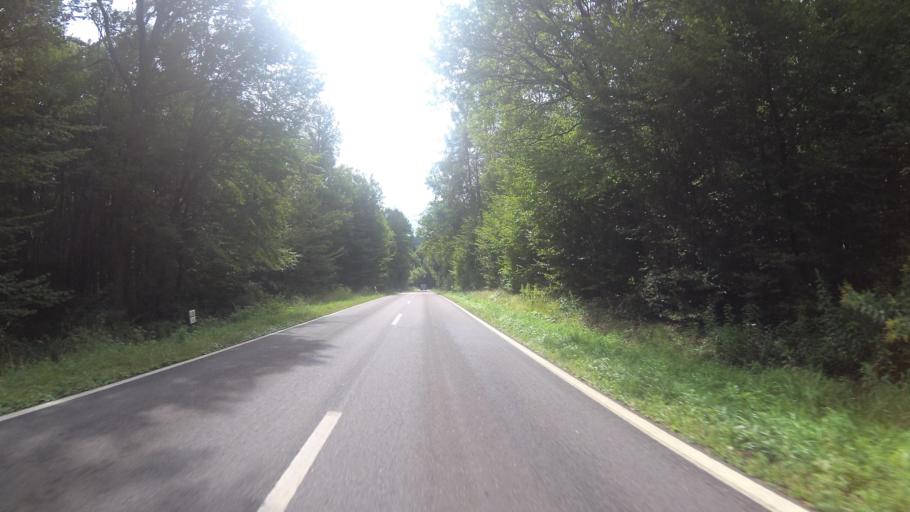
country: DE
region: Saarland
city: Saarbrucken
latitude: 49.2718
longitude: 6.9859
